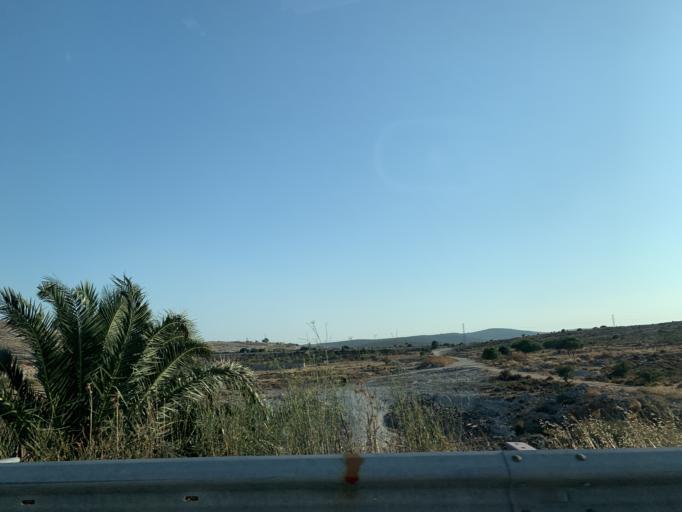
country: TR
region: Izmir
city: Alacati
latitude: 38.2807
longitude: 26.4015
